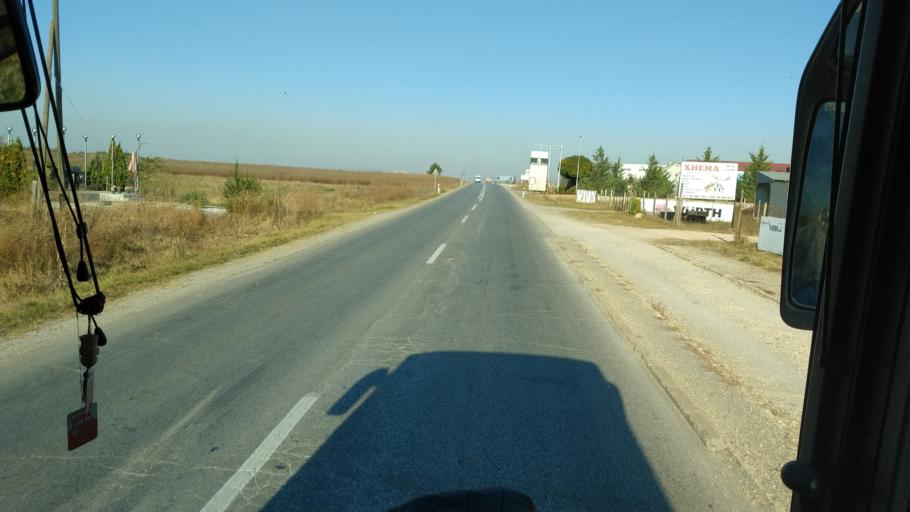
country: XK
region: Pristina
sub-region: Lipjan
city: Lipljan
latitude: 42.4893
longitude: 21.0956
